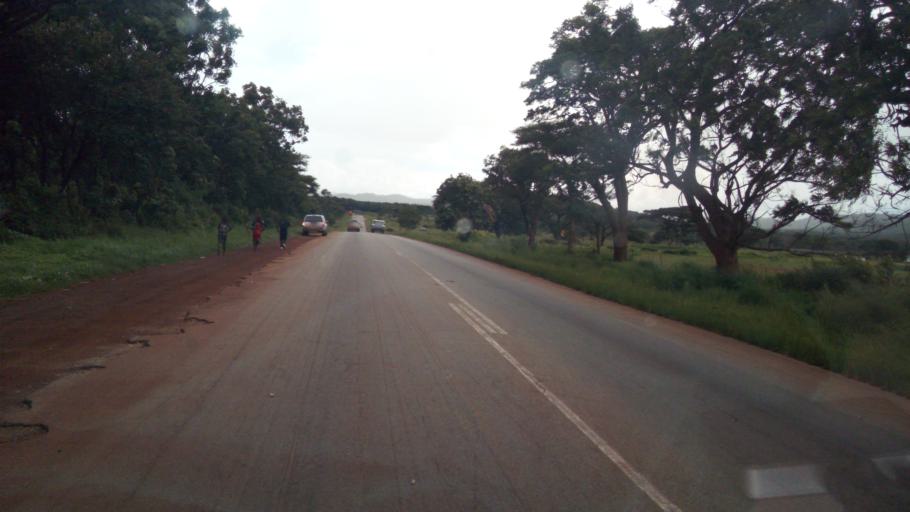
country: ZW
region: Mashonaland Central
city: Mazowe
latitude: -17.5826
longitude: 30.9695
